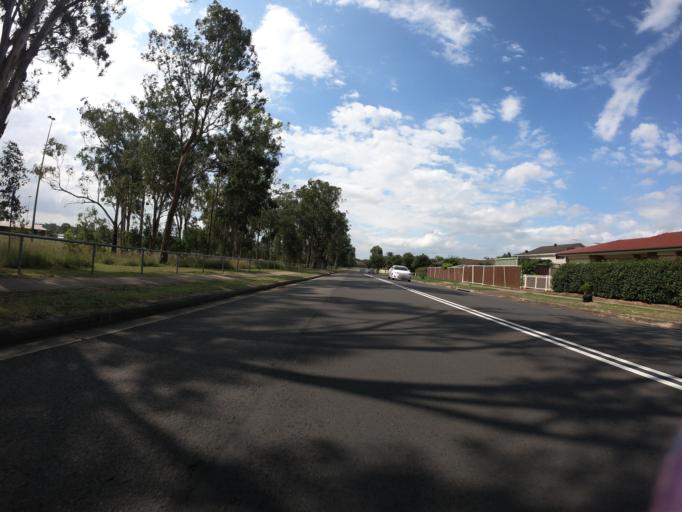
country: AU
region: New South Wales
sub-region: Blacktown
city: Hassall Grove
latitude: -33.7392
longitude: 150.8359
